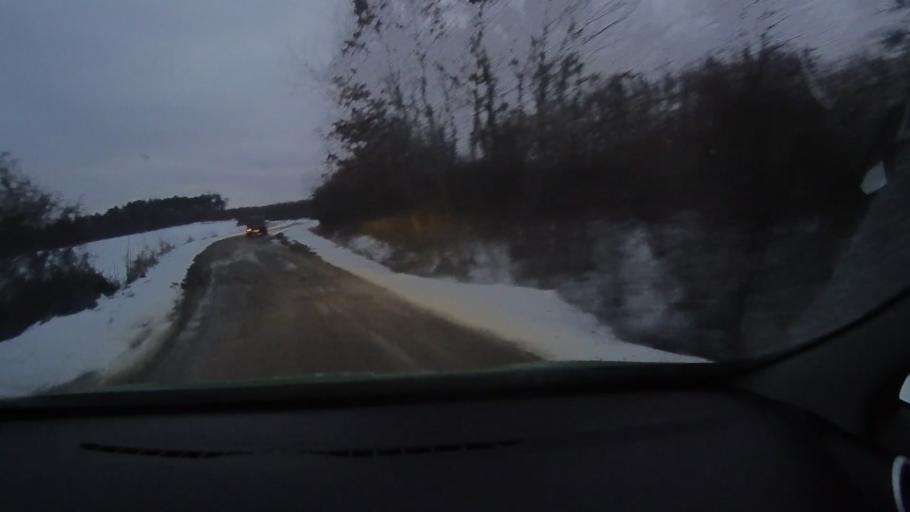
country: RO
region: Harghita
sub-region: Comuna Darjiu
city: Darjiu
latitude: 46.1863
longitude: 25.2472
